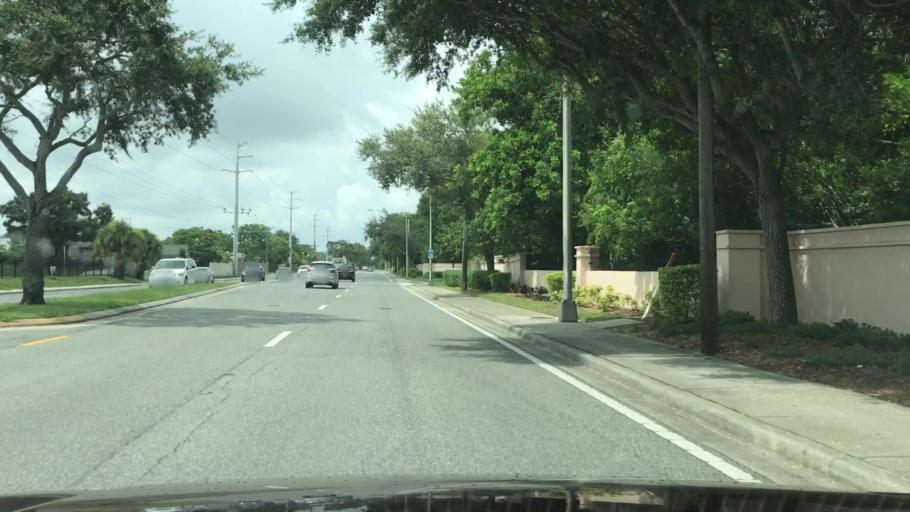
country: US
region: Florida
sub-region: Sarasota County
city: Gulf Gate Estates
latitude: 27.2419
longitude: -82.4975
